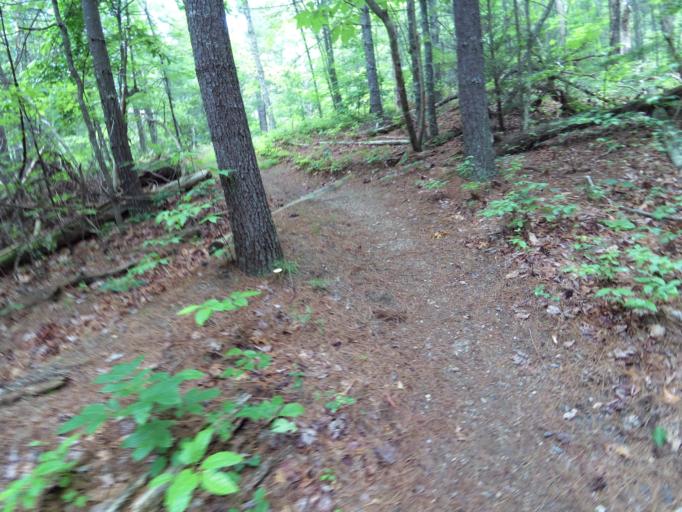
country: US
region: Tennessee
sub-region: Blount County
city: Wildwood
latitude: 35.6606
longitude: -83.8271
